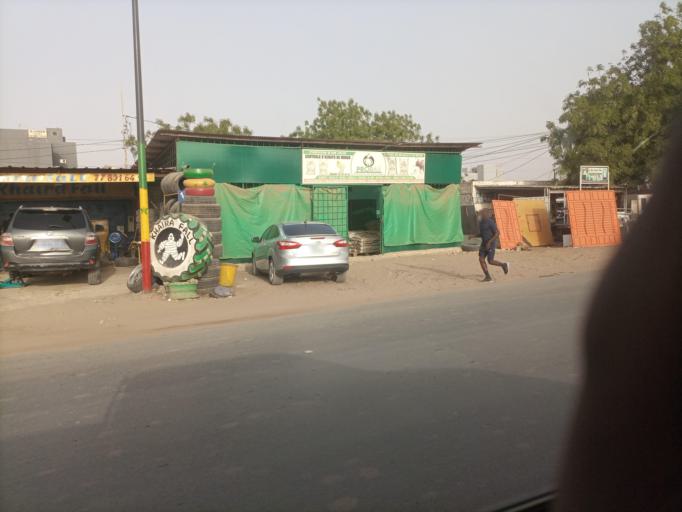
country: SN
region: Thies
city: Warang
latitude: 14.4389
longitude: -16.9782
